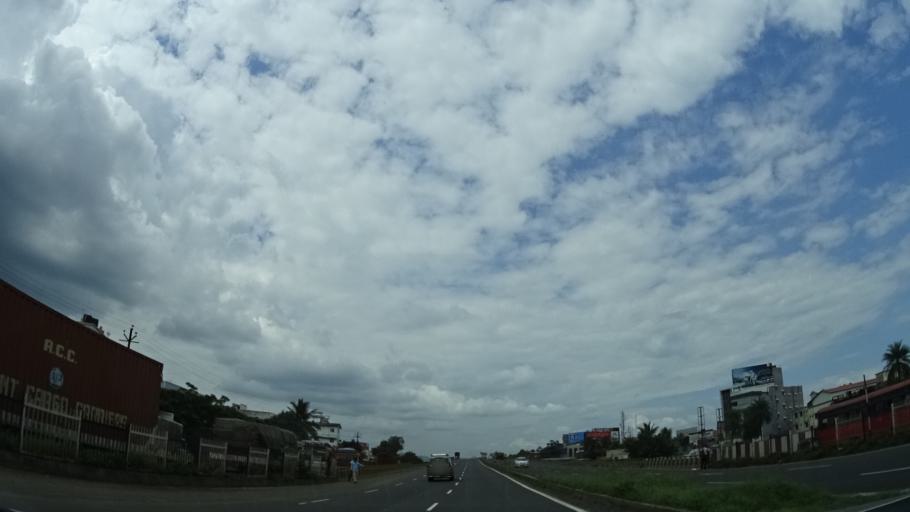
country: IN
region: Maharashtra
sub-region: Satara Division
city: Satara
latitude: 17.6829
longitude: 74.0231
